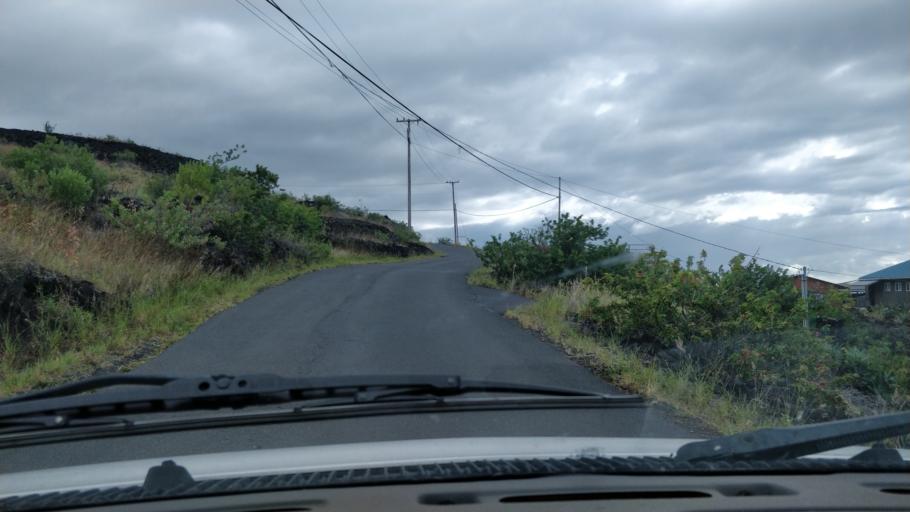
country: US
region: Hawaii
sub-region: Hawaii County
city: Hawaiian Ocean View
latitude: 19.2030
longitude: -155.8910
